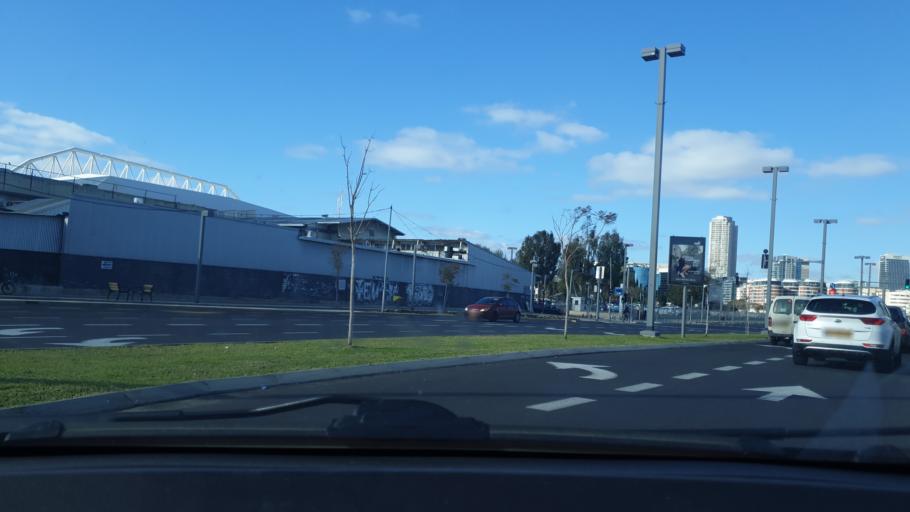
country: IL
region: Tel Aviv
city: Yafo
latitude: 32.0491
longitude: 34.7638
